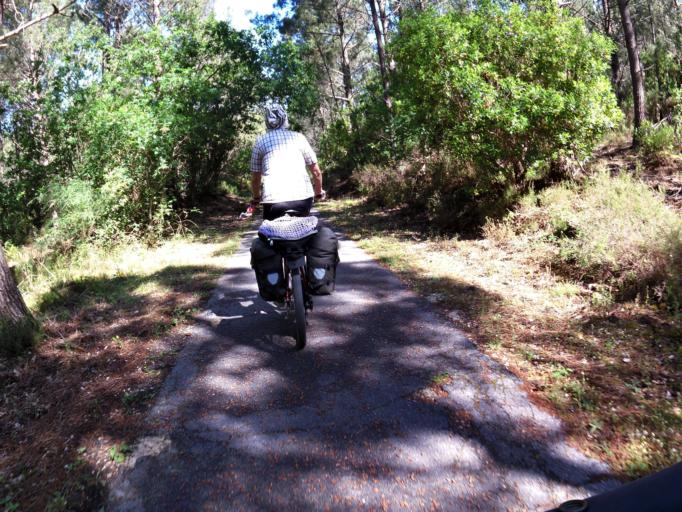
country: FR
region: Aquitaine
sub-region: Departement de la Gironde
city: Lacanau
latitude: 45.0308
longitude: -1.1554
